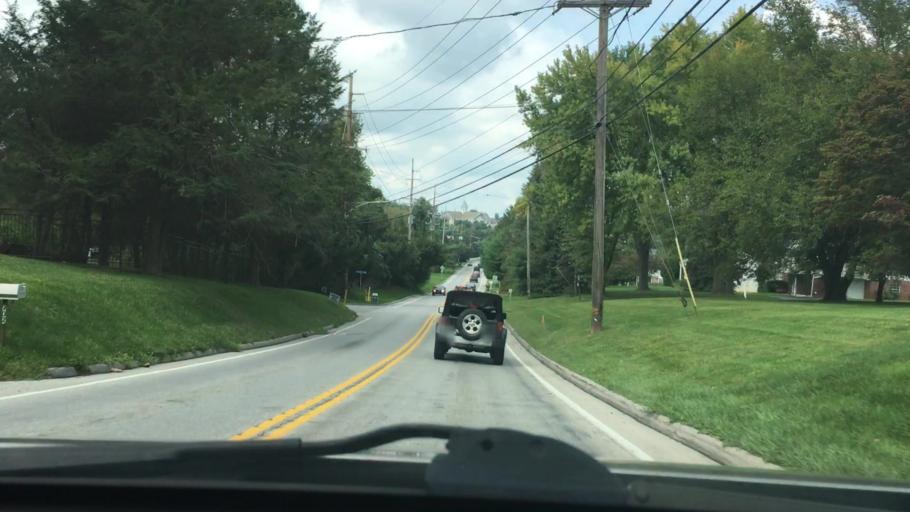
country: US
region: Pennsylvania
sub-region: Chester County
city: Malvern
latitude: 39.9590
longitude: -75.5174
